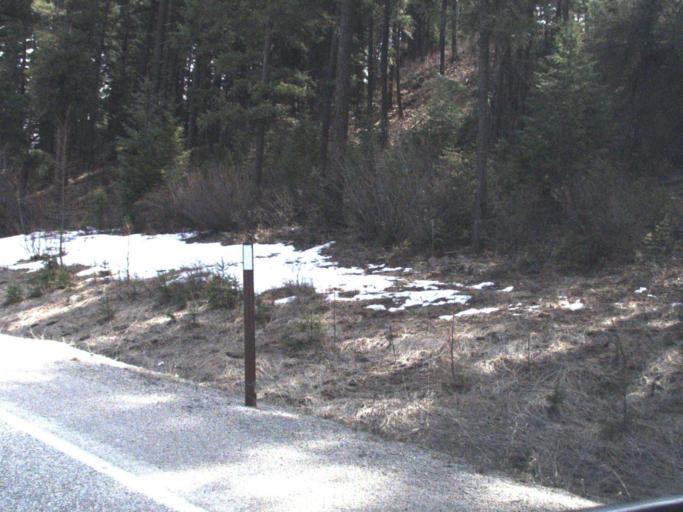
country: US
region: Washington
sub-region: Stevens County
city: Colville
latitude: 48.5154
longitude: -117.7572
